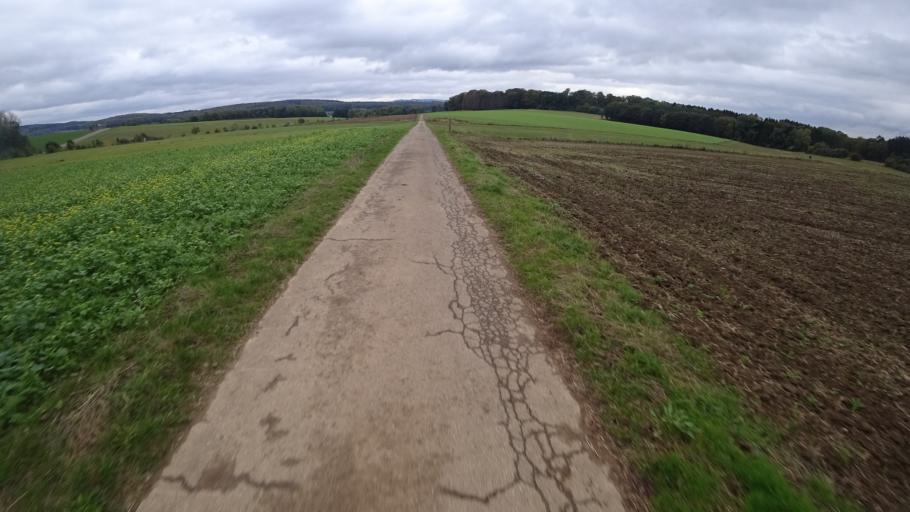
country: DE
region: Rheinland-Pfalz
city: Maxsain
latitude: 50.5602
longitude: 7.7784
